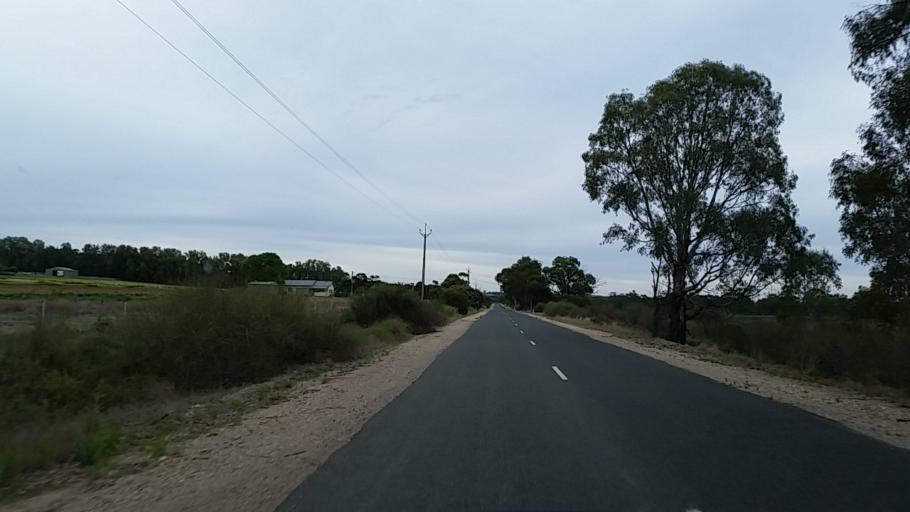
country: AU
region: South Australia
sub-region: Mid Murray
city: Mannum
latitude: -34.7591
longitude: 139.5649
